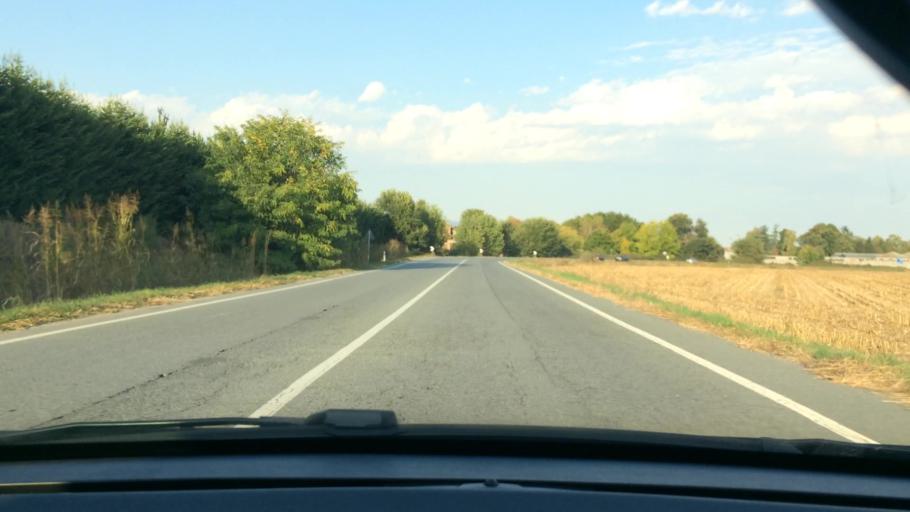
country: IT
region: Piedmont
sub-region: Provincia di Torino
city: Candiolo
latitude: 44.9540
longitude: 7.5912
